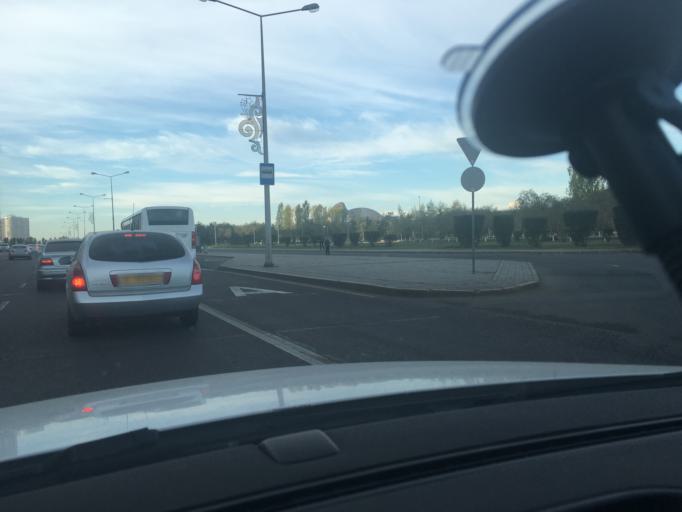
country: KZ
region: Astana Qalasy
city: Astana
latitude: 51.1334
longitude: 71.4597
